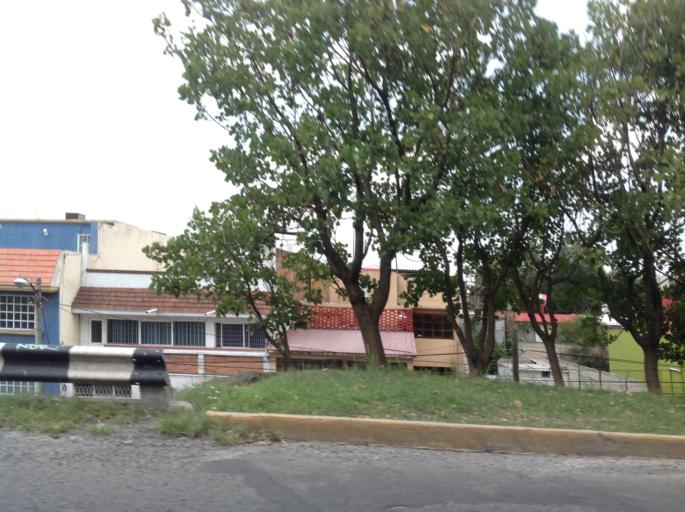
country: MX
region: Mexico
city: Ciudad Lopez Mateos
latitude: 19.5961
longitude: -99.2286
